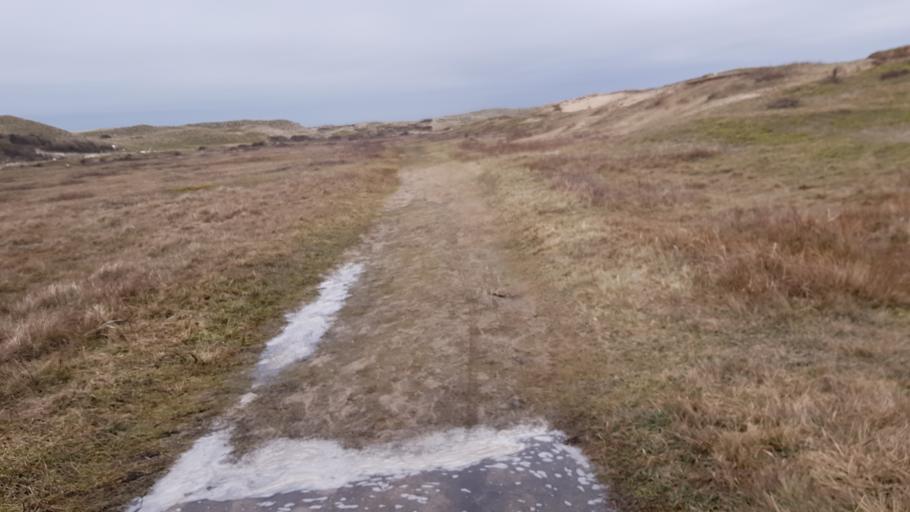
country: NL
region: North Holland
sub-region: Gemeente Bergen
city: Egmond aan Zee
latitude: 52.5826
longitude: 4.6170
